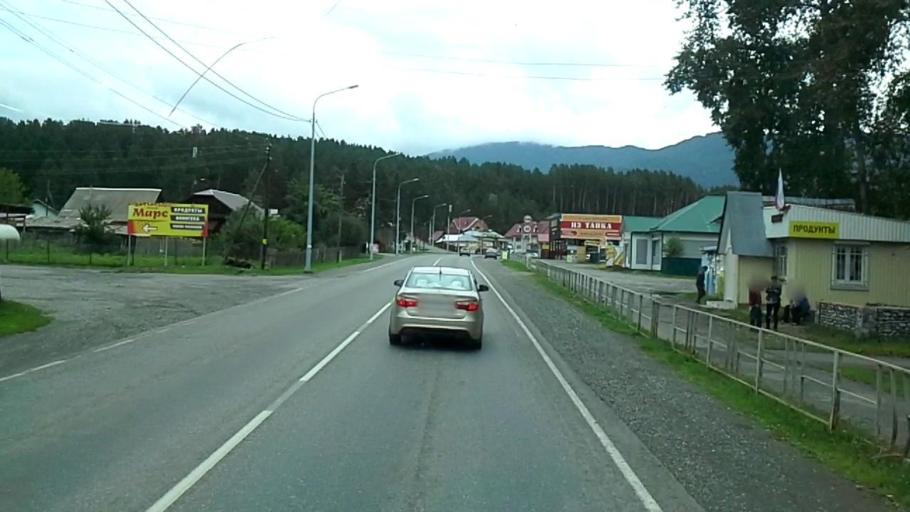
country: RU
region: Altay
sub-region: Mayminskiy Rayon
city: Manzherok
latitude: 51.8337
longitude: 85.7771
